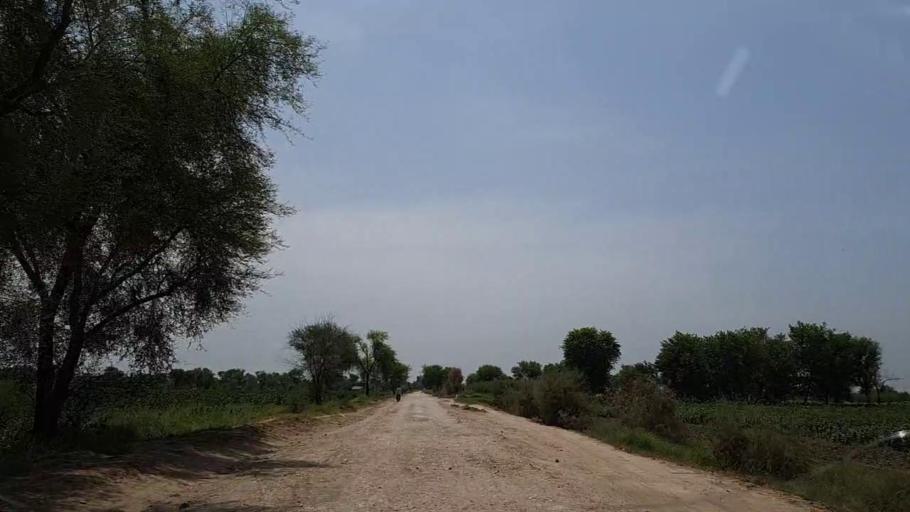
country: PK
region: Sindh
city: Khanpur
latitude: 27.8591
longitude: 69.4868
